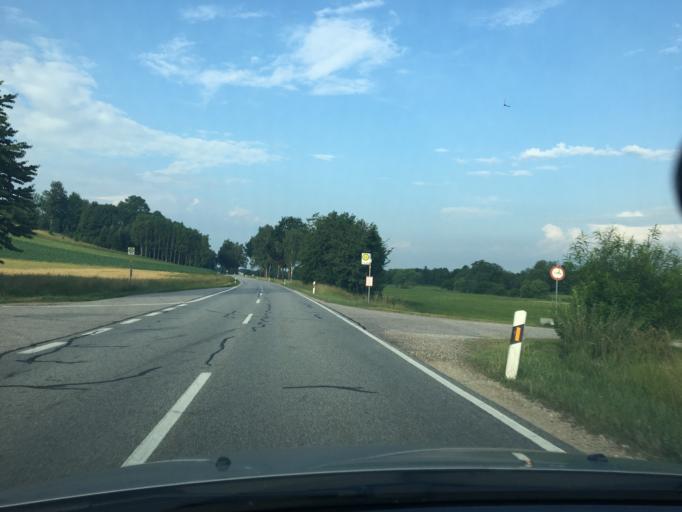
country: DE
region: Bavaria
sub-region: Lower Bavaria
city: Vilsbiburg
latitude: 48.4244
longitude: 12.3451
